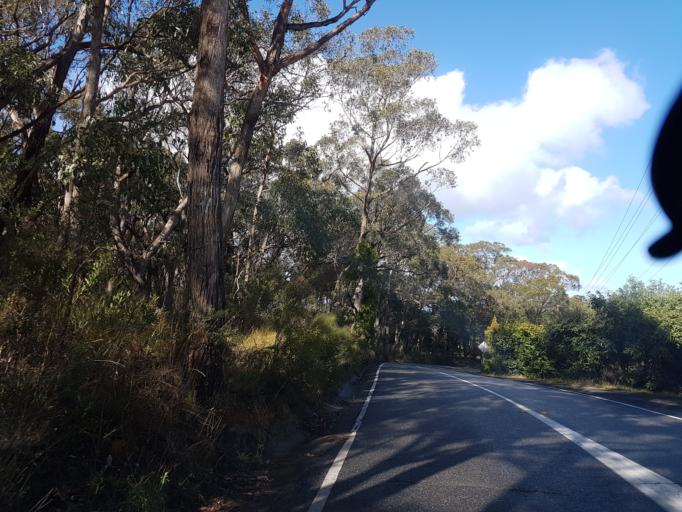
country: AU
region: South Australia
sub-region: Adelaide Hills
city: Heathfield
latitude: -35.0245
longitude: 138.7156
